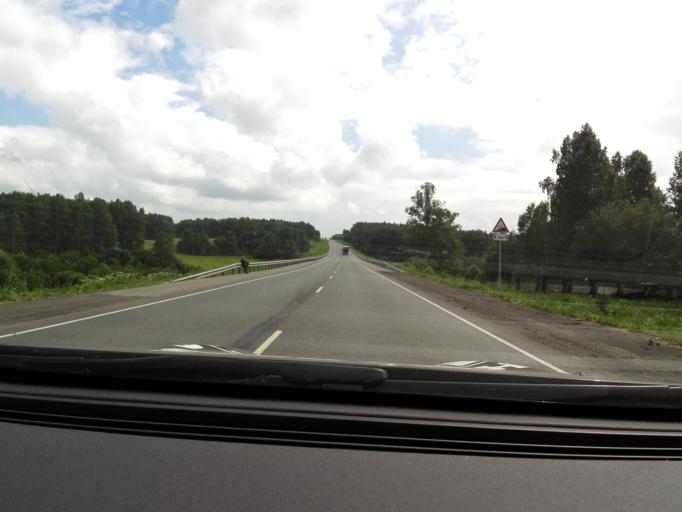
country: RU
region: Perm
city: Ust'-Kishert'
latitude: 57.1808
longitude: 57.1305
